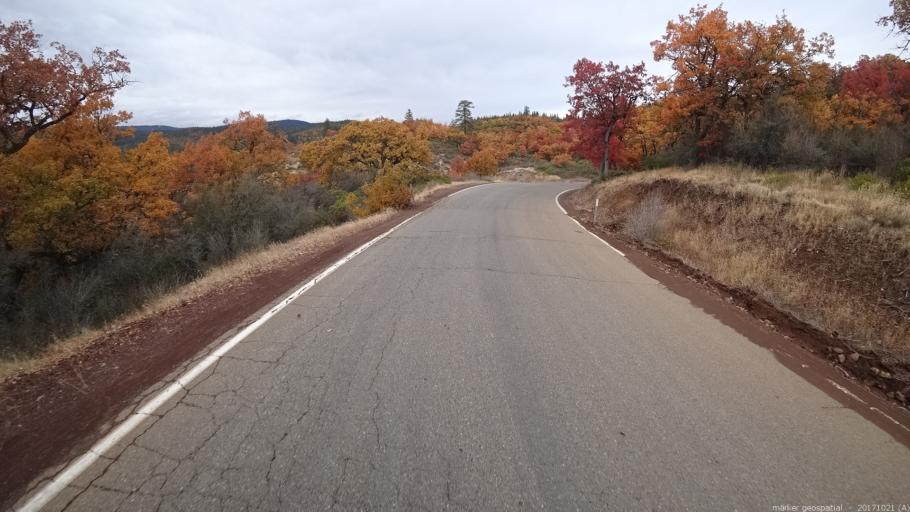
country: US
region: California
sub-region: Shasta County
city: Burney
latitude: 41.0423
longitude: -121.6656
